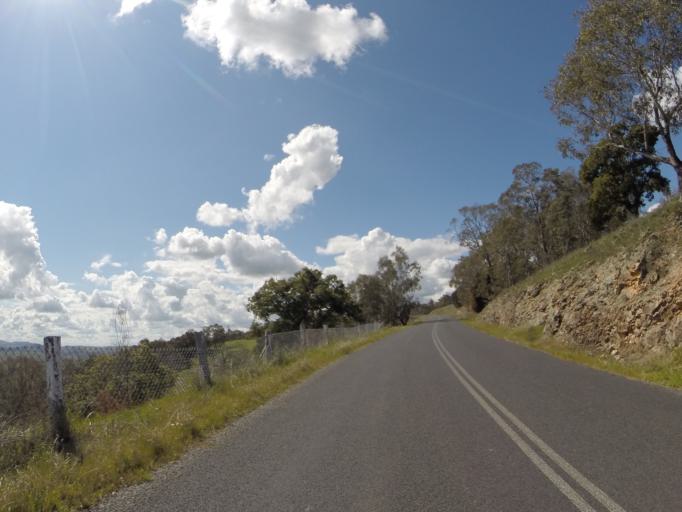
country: AU
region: New South Wales
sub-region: Yass Valley
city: Yass
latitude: -34.9863
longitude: 148.8410
